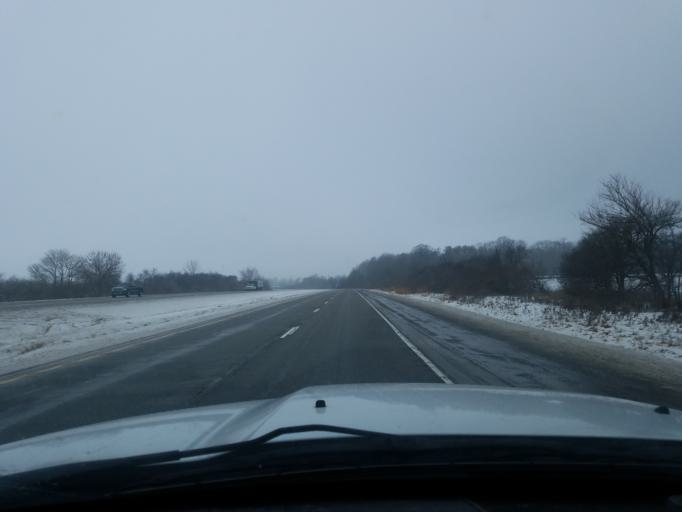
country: US
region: Indiana
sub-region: Fulton County
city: Rochester
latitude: 41.0379
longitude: -86.1937
